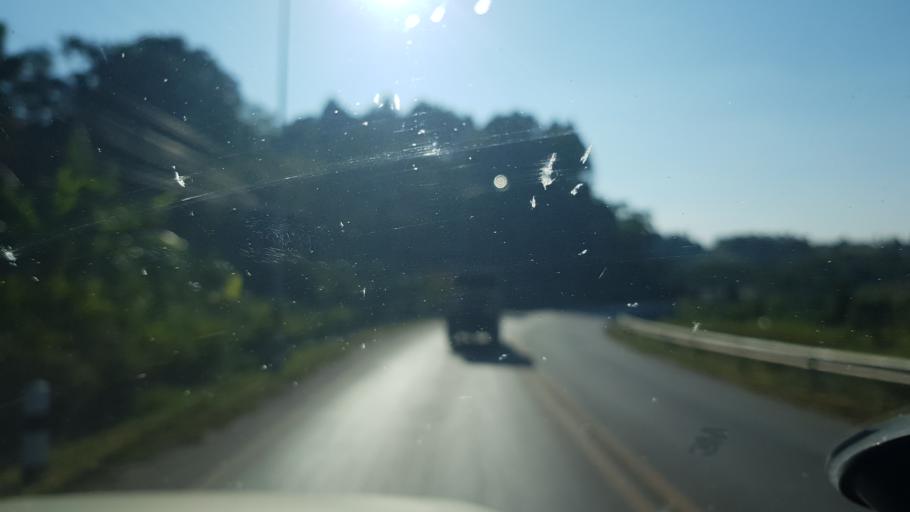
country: TH
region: Phetchabun
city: Khao Kho
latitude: 16.6481
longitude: 101.0093
